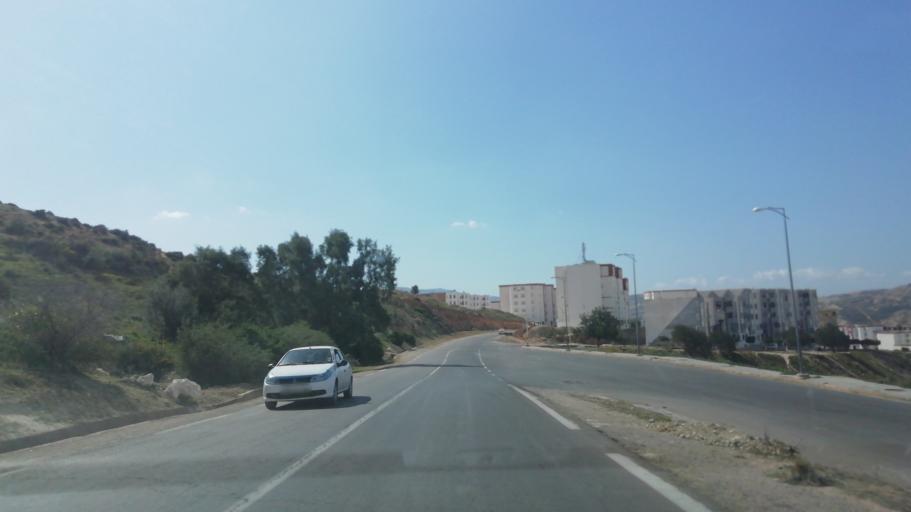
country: DZ
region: Mascara
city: Mascara
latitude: 35.5567
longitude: 0.0736
